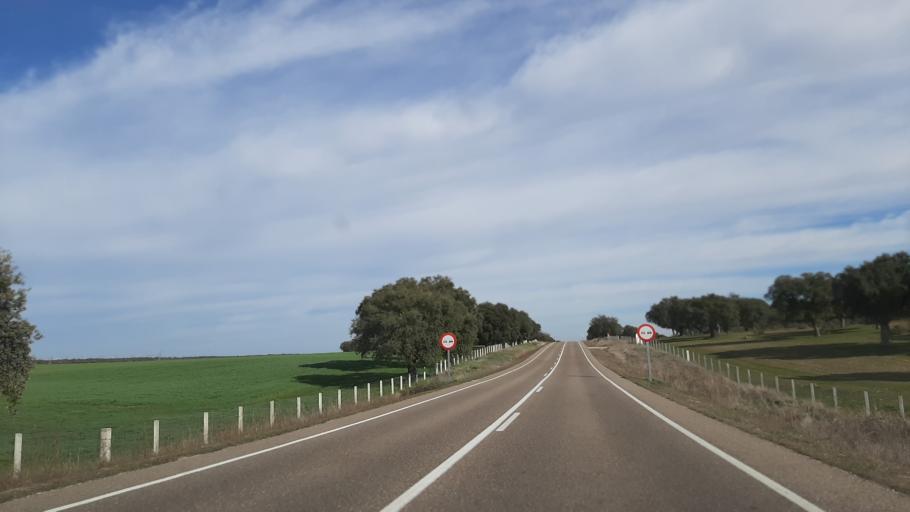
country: ES
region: Castille and Leon
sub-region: Provincia de Salamanca
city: Anover de Tormes
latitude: 41.0895
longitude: -5.9378
